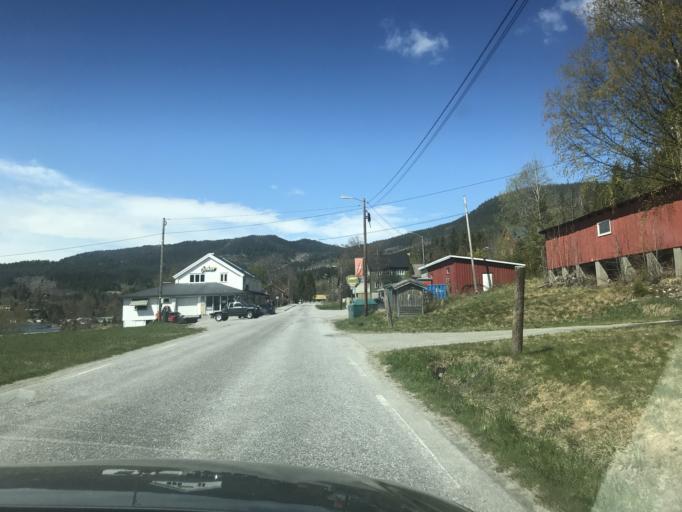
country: NO
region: Telemark
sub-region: Hjartdal
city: Sauland
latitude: 59.7505
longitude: 8.7993
